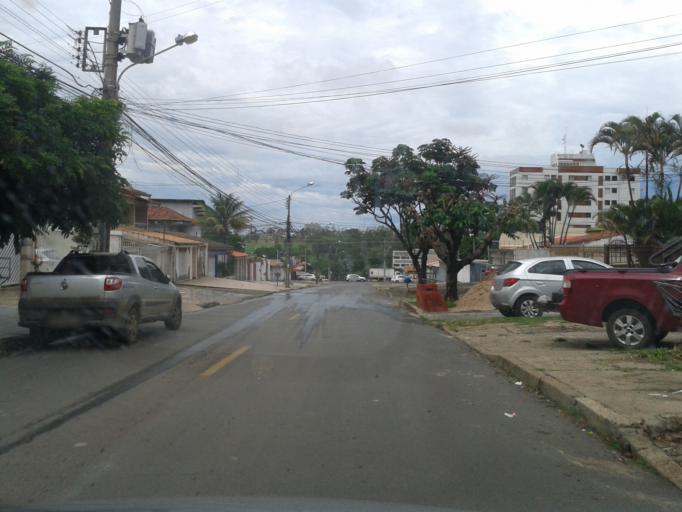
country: BR
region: Federal District
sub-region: Brasilia
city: Brasilia
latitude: -15.8287
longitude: -48.0609
